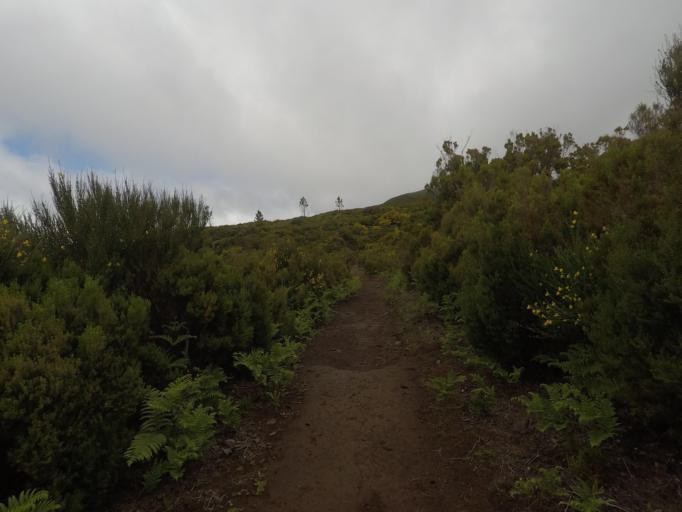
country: PT
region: Madeira
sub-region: Calheta
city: Arco da Calheta
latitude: 32.7737
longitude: -17.1326
